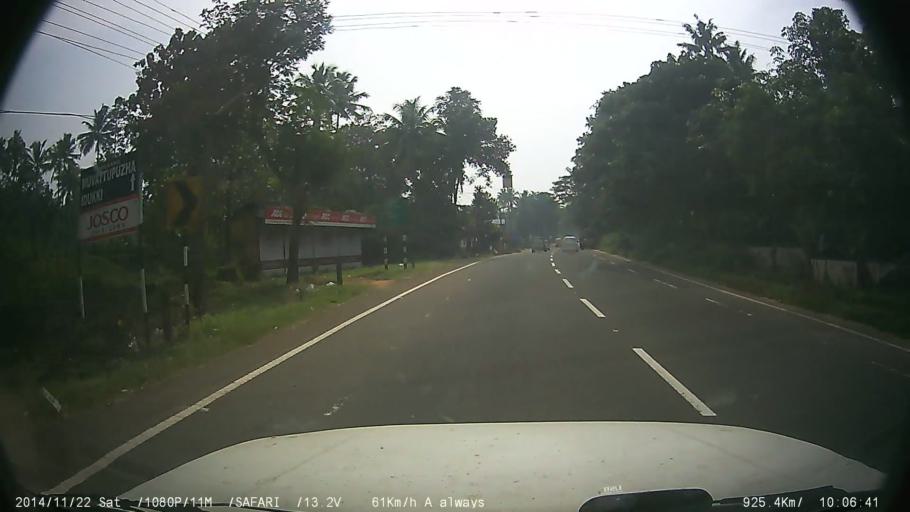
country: IN
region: Kerala
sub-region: Ernakulam
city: Muvattupula
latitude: 10.0444
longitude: 76.5347
